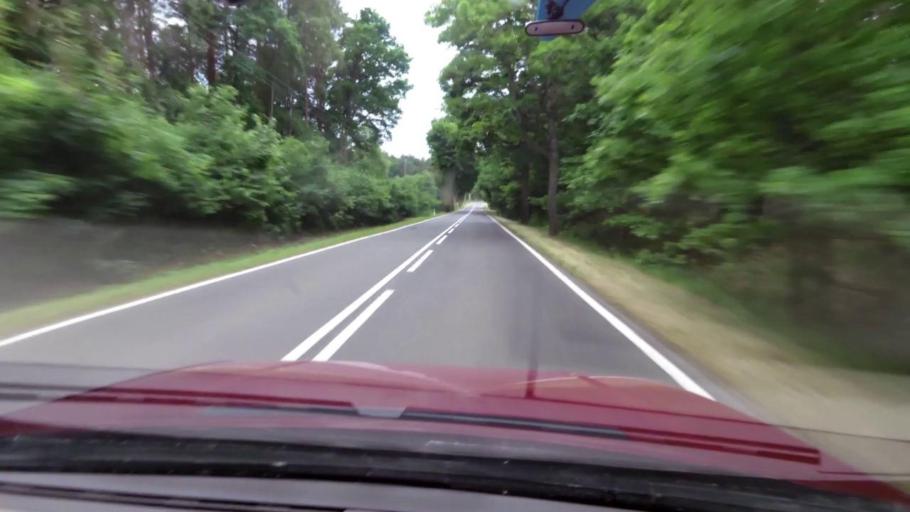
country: PL
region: West Pomeranian Voivodeship
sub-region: Powiat koszalinski
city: Sianow
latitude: 54.1824
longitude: 16.3346
